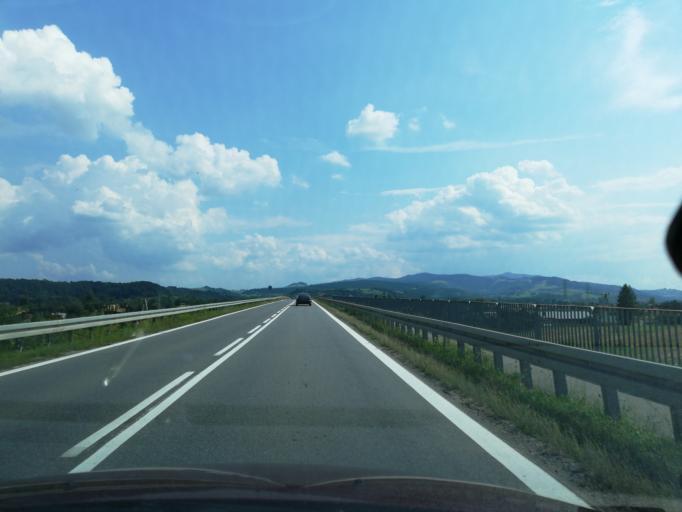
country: PL
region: Lesser Poland Voivodeship
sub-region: Powiat nowosadecki
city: Stary Sacz
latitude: 49.5744
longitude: 20.6451
